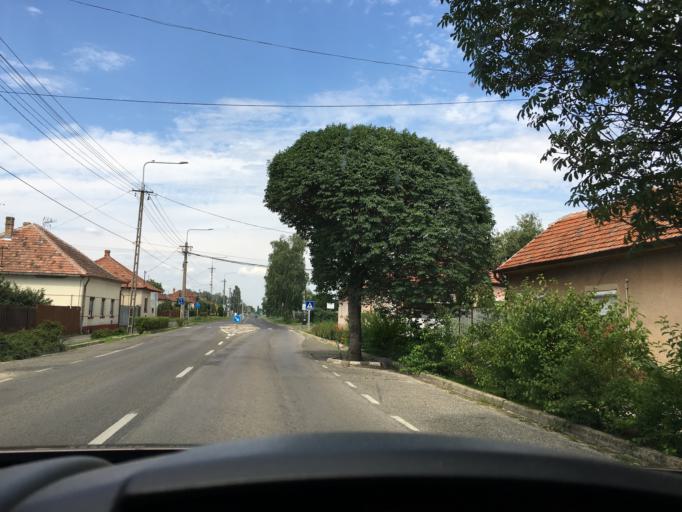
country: HU
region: Csongrad
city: Morahalom
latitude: 46.2170
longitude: 19.8787
